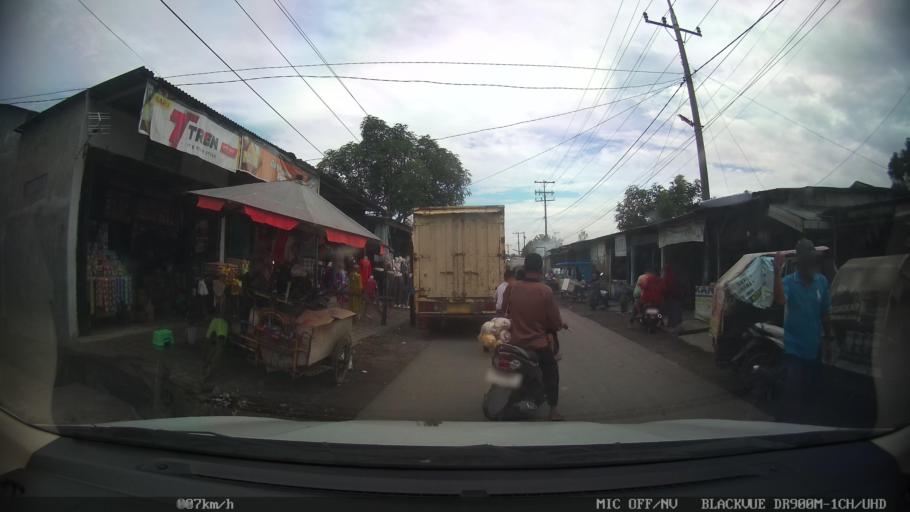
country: ID
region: North Sumatra
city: Sunggal
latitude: 3.6118
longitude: 98.5803
